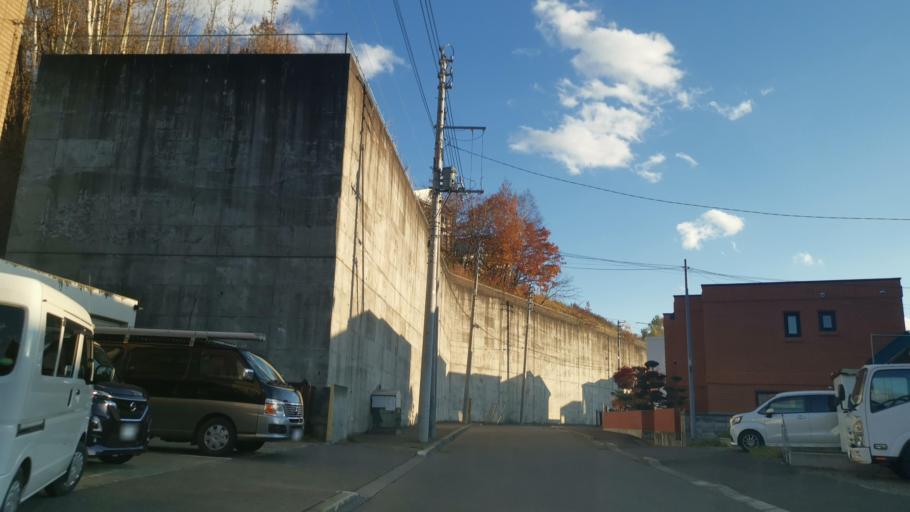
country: JP
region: Hokkaido
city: Sapporo
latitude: 42.9972
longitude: 141.3659
